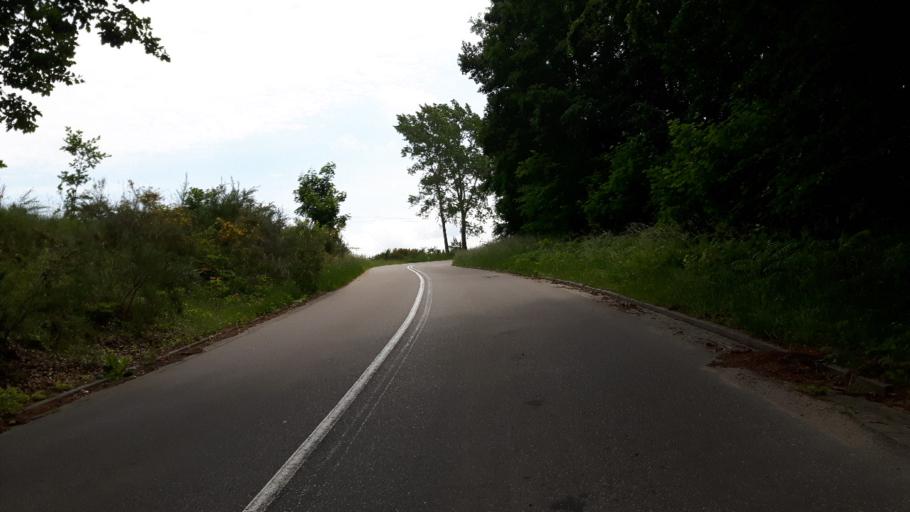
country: PL
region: Pomeranian Voivodeship
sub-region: Powiat leborski
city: Leba
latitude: 54.7548
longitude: 17.7085
